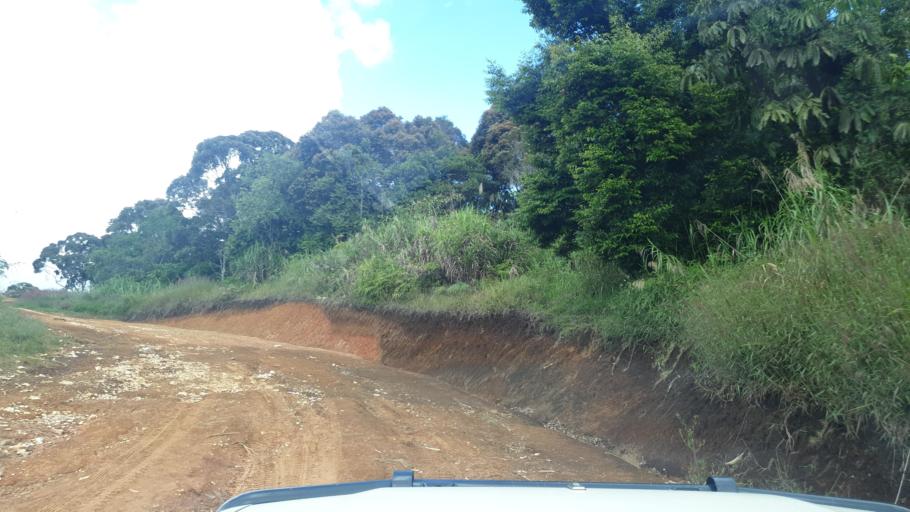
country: PG
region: Eastern Highlands
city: Goroka
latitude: -6.2798
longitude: 145.1933
